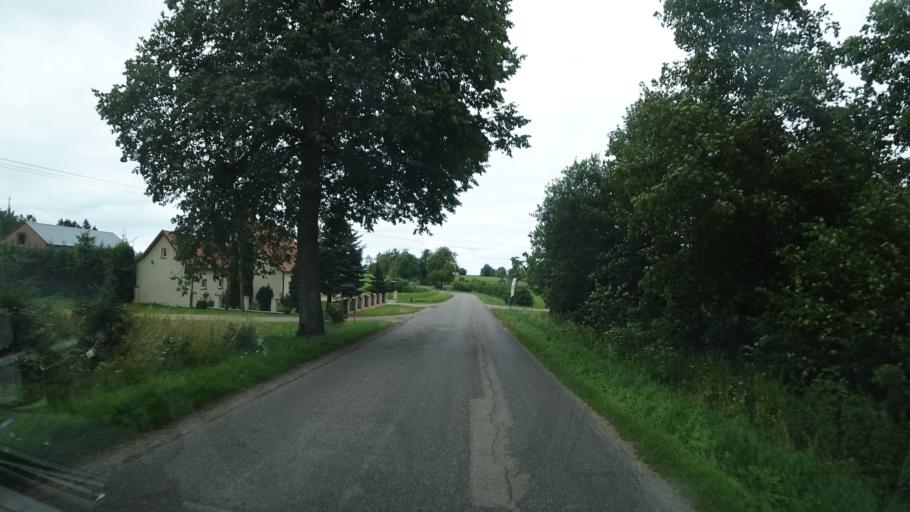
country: PL
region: Podlasie
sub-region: Powiat suwalski
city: Filipow
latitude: 54.2825
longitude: 22.5389
